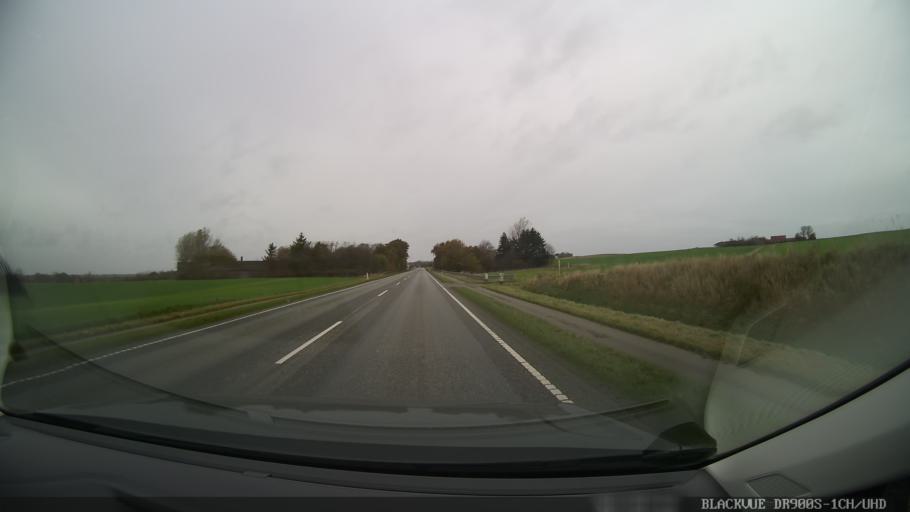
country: DK
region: North Denmark
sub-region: Thisted Kommune
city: Thisted
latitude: 56.8623
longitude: 8.6874
